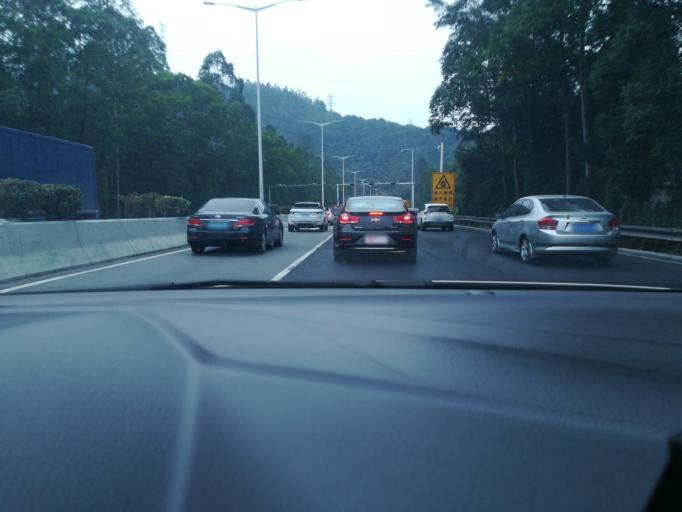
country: CN
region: Guangdong
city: Longdong
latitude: 23.2253
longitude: 113.3566
